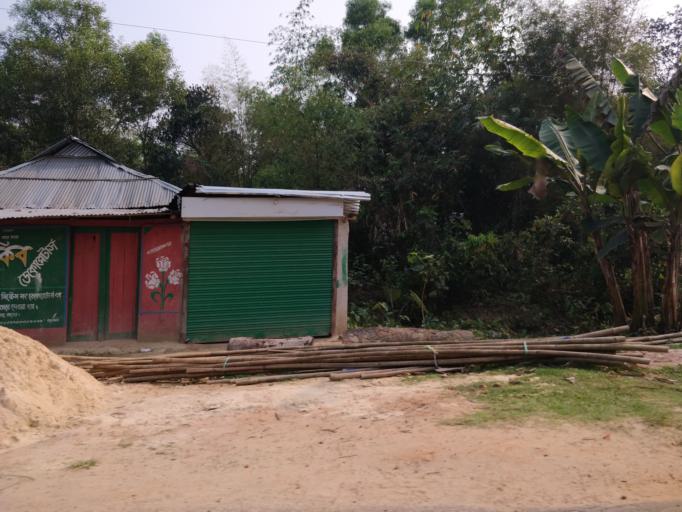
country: IN
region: Tripura
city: Khowai
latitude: 24.1296
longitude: 91.3761
